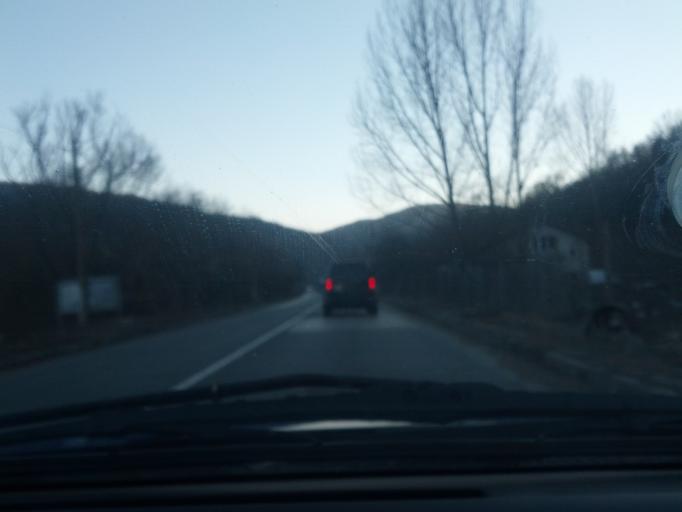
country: BG
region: Vratsa
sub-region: Obshtina Mezdra
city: Mezdra
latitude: 43.0626
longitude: 23.6847
